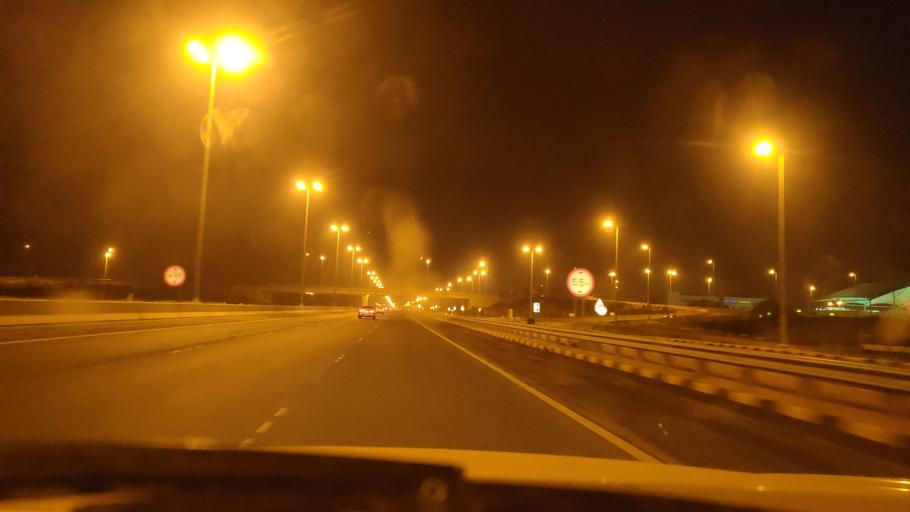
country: KW
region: Muhafazat al Jahra'
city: Al Jahra'
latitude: 29.3418
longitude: 47.7106
